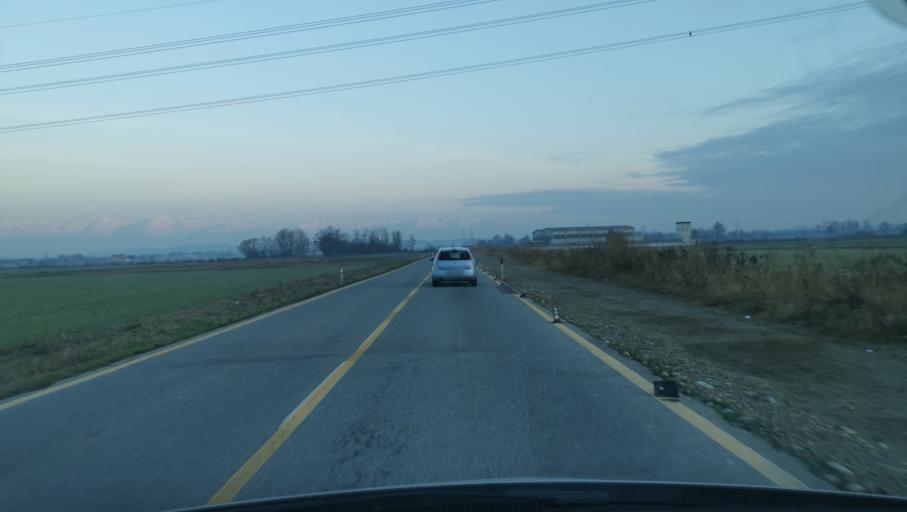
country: IT
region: Piedmont
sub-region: Provincia di Torino
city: Montanaro
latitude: 45.2585
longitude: 7.8920
